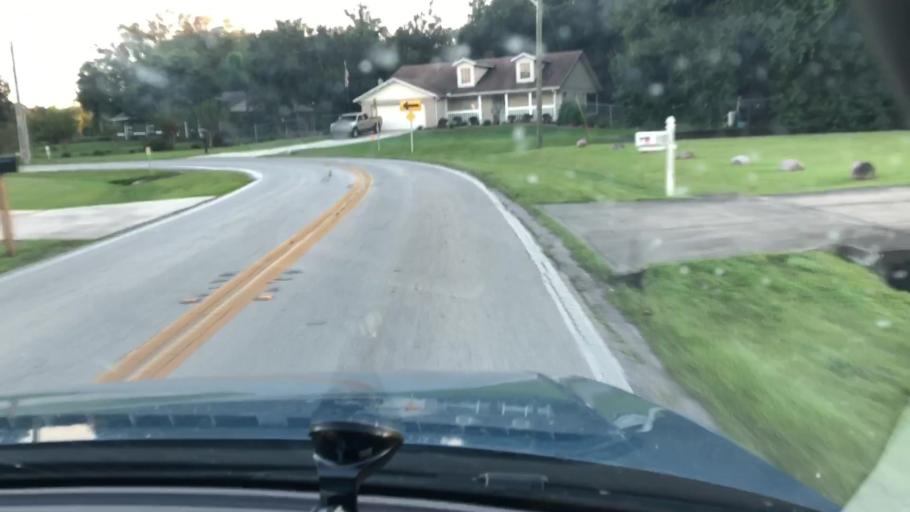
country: US
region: Florida
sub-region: Polk County
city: Kathleen
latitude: 28.1248
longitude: -82.0405
